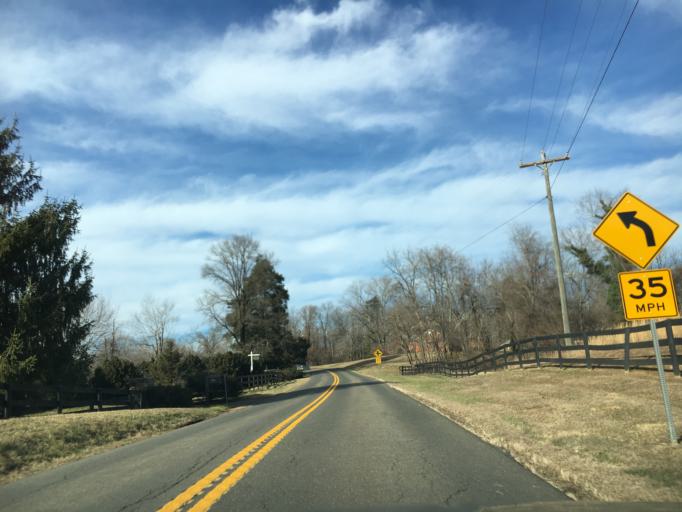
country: US
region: Virginia
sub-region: Fauquier County
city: Marshall
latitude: 38.7806
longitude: -77.9828
